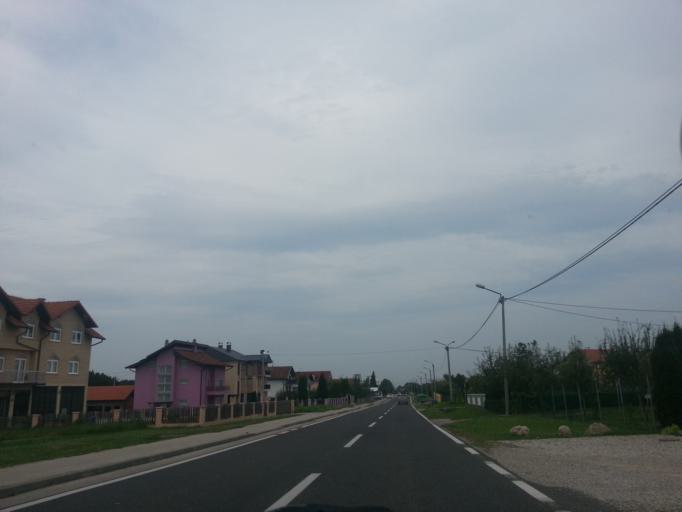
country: BA
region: Brcko
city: Brcko
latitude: 44.8283
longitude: 18.8187
